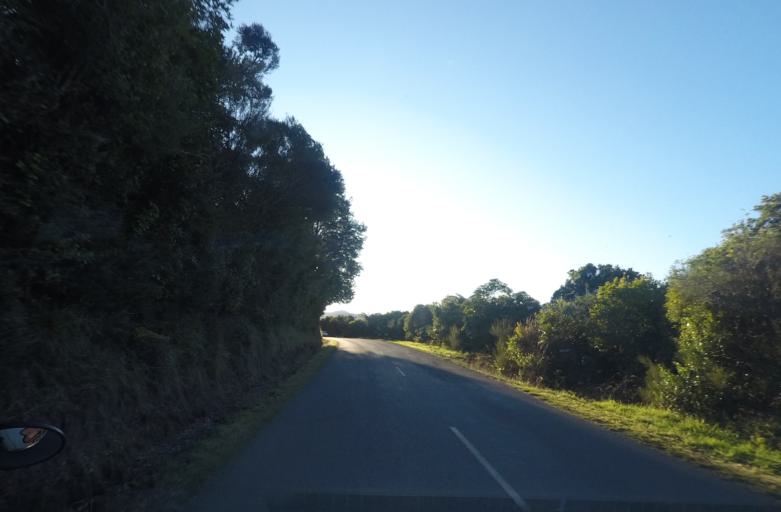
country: NZ
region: Marlborough
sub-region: Marlborough District
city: Picton
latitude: -41.2912
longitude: 173.8188
